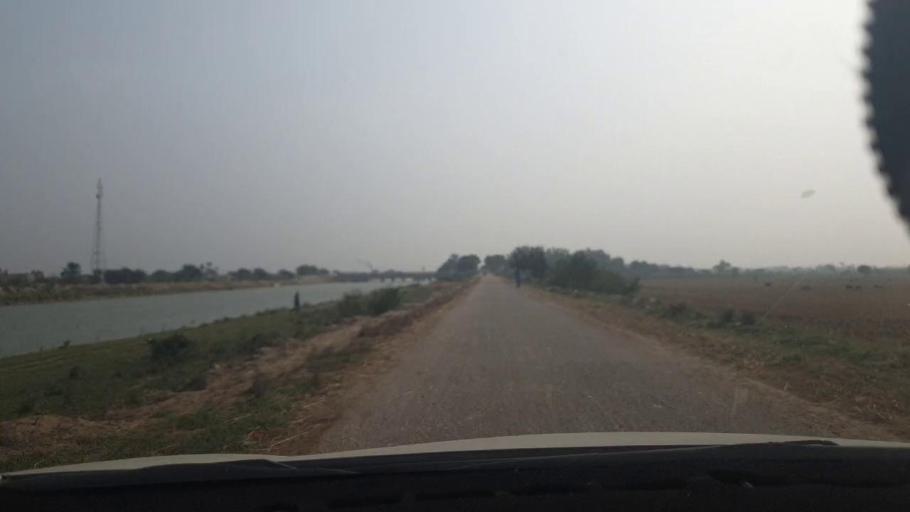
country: PK
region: Sindh
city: Tando Muhammad Khan
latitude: 24.9618
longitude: 68.4959
